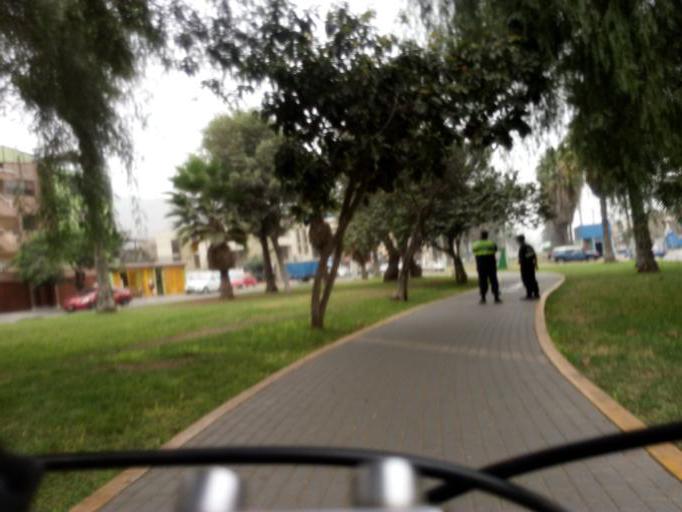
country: PE
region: Lima
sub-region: Lima
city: La Molina
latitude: -12.0663
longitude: -76.9389
